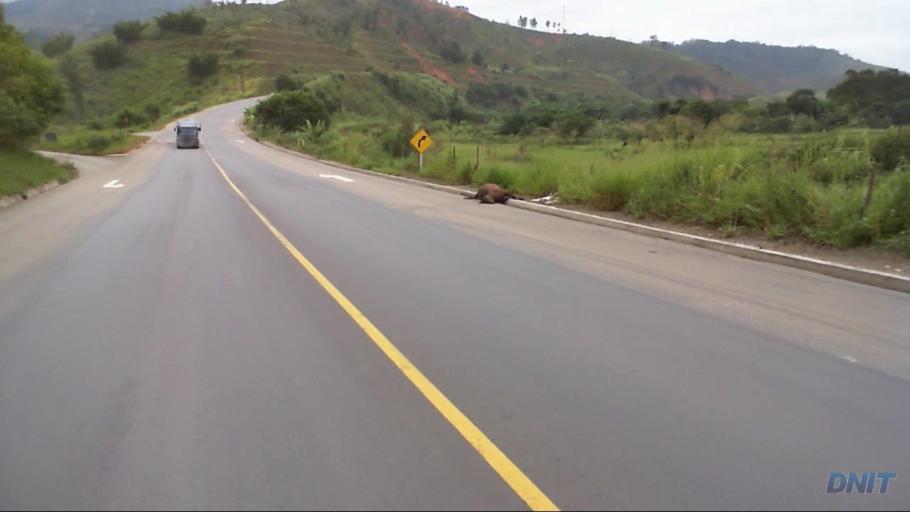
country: BR
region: Minas Gerais
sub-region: Coronel Fabriciano
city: Coronel Fabriciano
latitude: -19.5327
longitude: -42.6725
